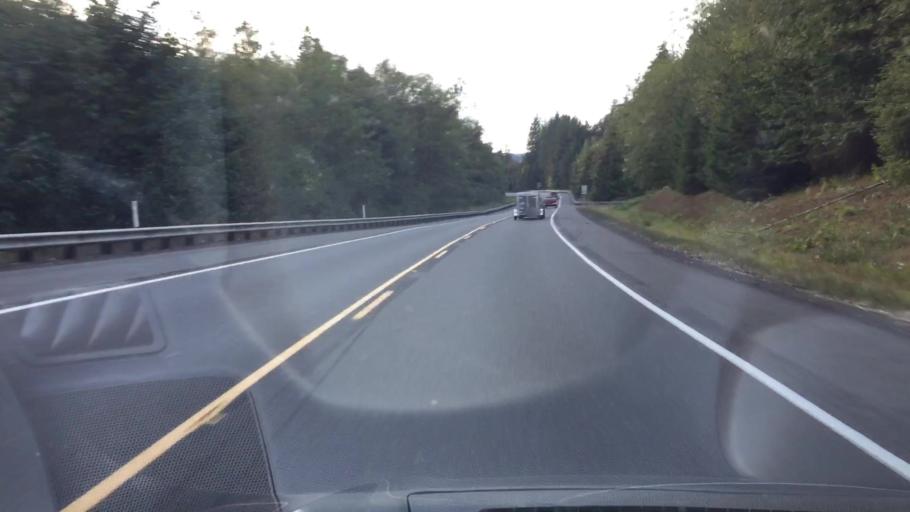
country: US
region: Washington
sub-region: Lewis County
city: Morton
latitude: 46.5331
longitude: -122.5375
